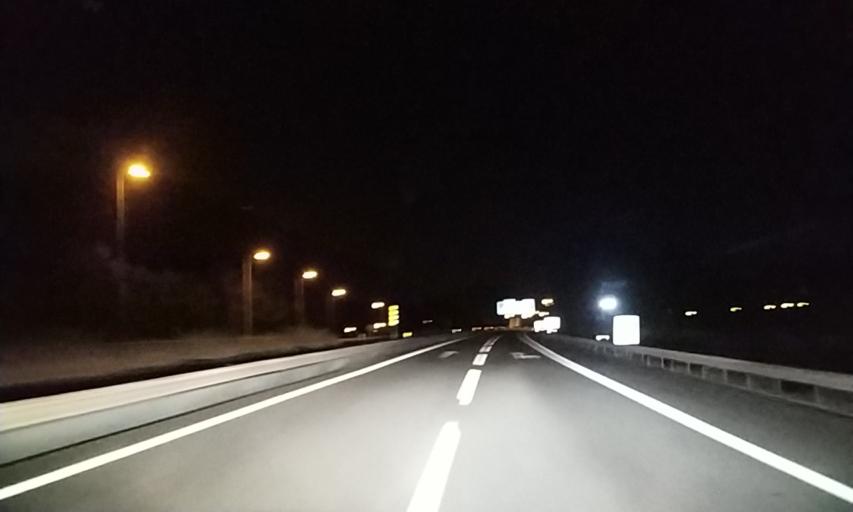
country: PT
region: Aveiro
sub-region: Albergaria-A-Velha
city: Albergaria-a-Velha
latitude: 40.6890
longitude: -8.5210
